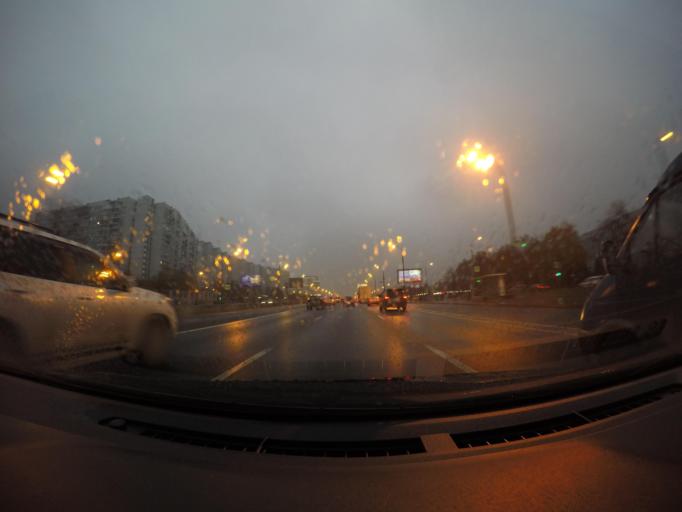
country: RU
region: Moscow
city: Nagornyy
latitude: 55.6248
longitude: 37.6162
